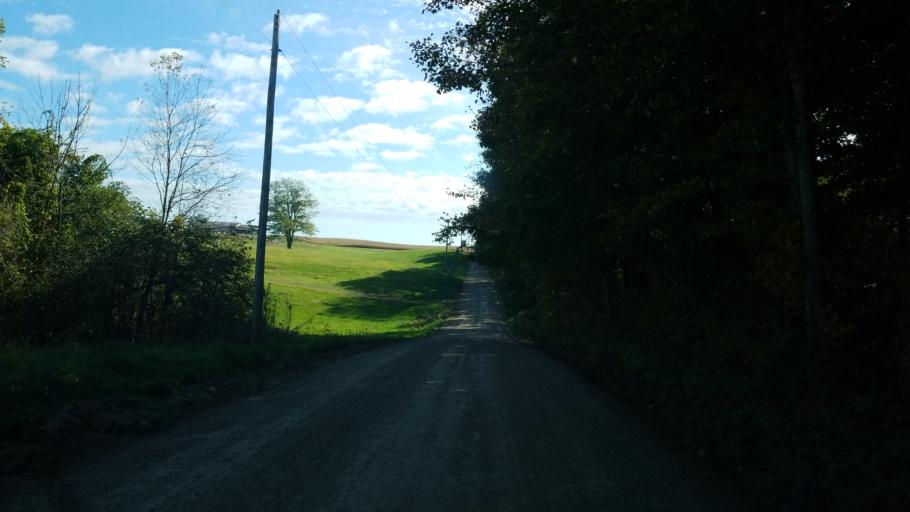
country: US
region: Ohio
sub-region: Morrow County
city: Mount Gilead
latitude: 40.5360
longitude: -82.6992
